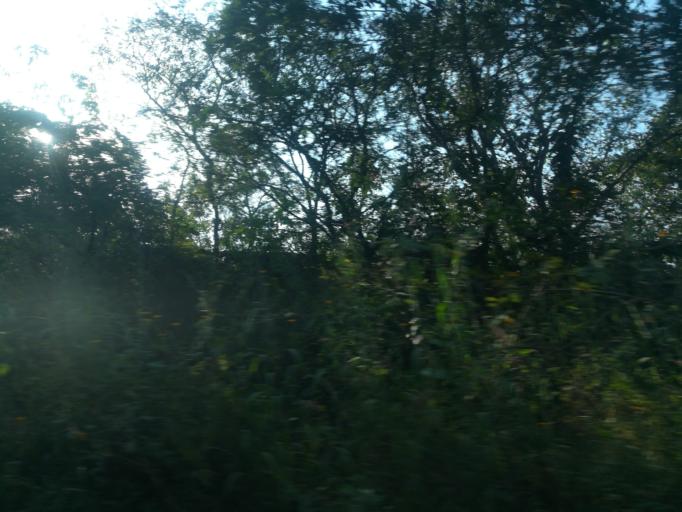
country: NG
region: Ogun
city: Abeokuta
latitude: 7.2284
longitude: 3.3008
